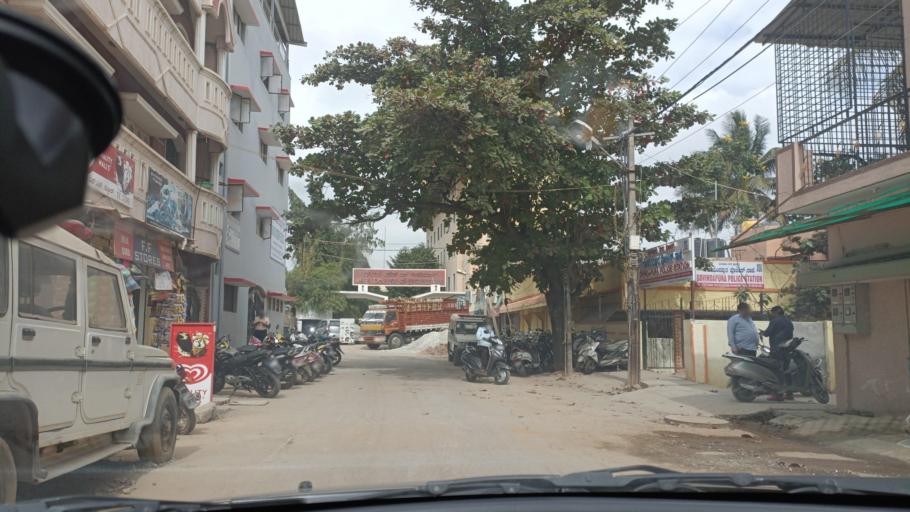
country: IN
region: Karnataka
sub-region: Bangalore Urban
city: Bangalore
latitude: 13.0341
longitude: 77.6192
